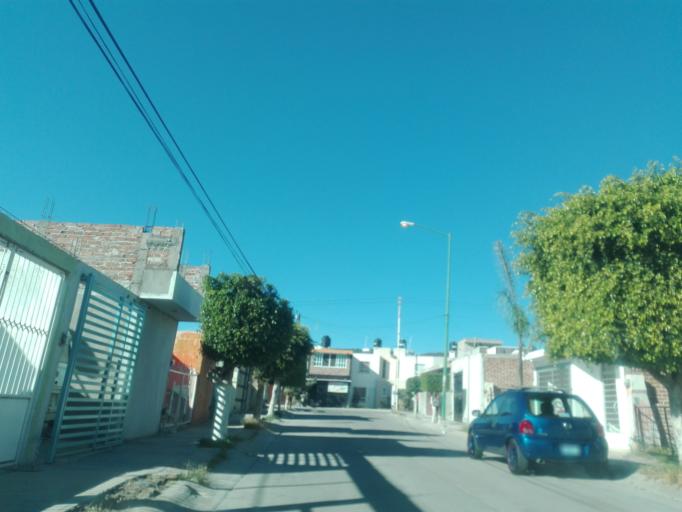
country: MX
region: Guanajuato
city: Leon
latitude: 21.1947
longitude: -101.6751
